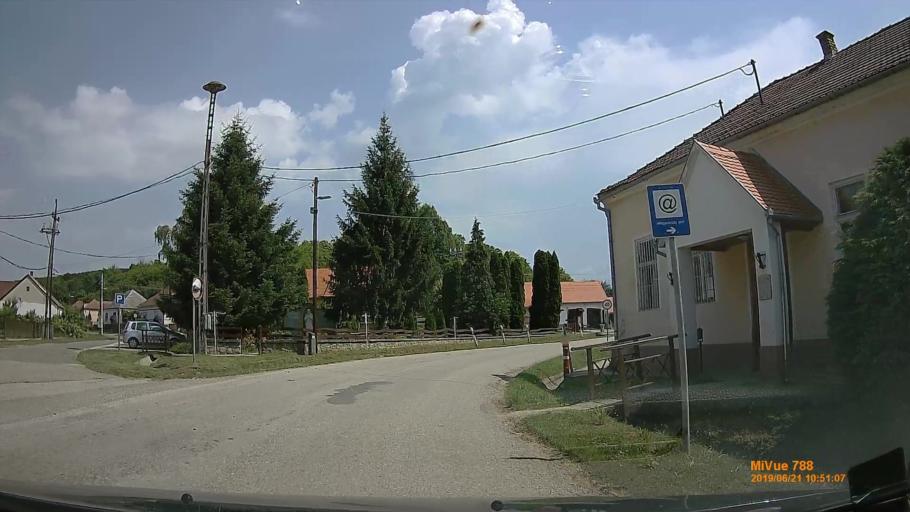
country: HU
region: Baranya
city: Buekkoesd
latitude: 46.1337
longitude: 18.0443
